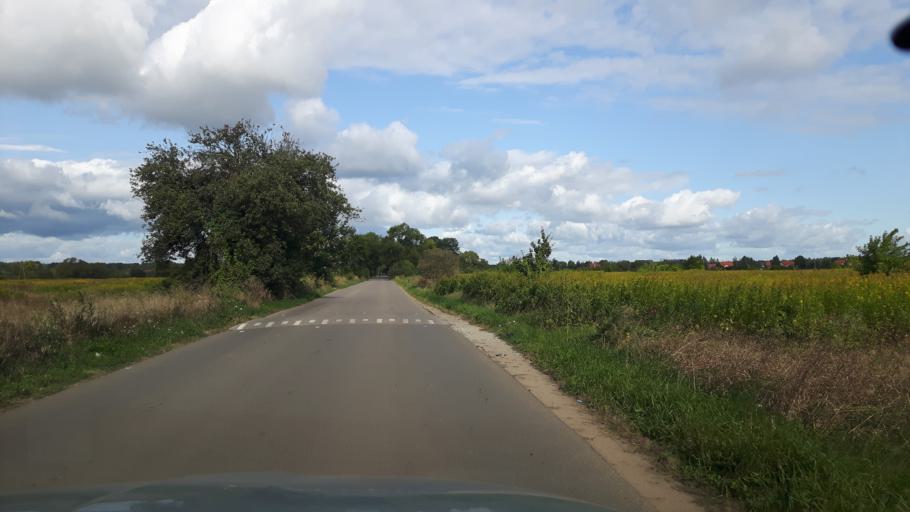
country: PL
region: Masovian Voivodeship
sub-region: Powiat wolominski
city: Marki
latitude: 52.3320
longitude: 21.0738
